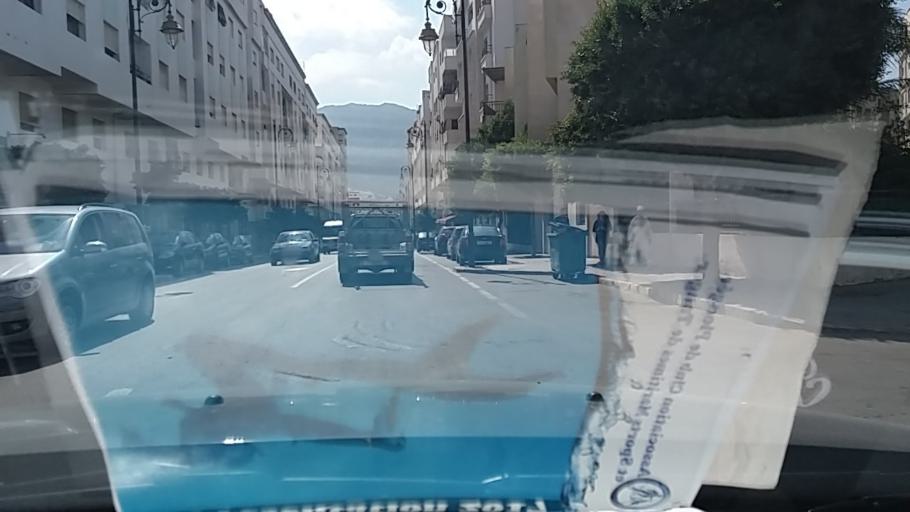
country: MA
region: Tanger-Tetouan
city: Tetouan
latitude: 35.5673
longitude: -5.3569
